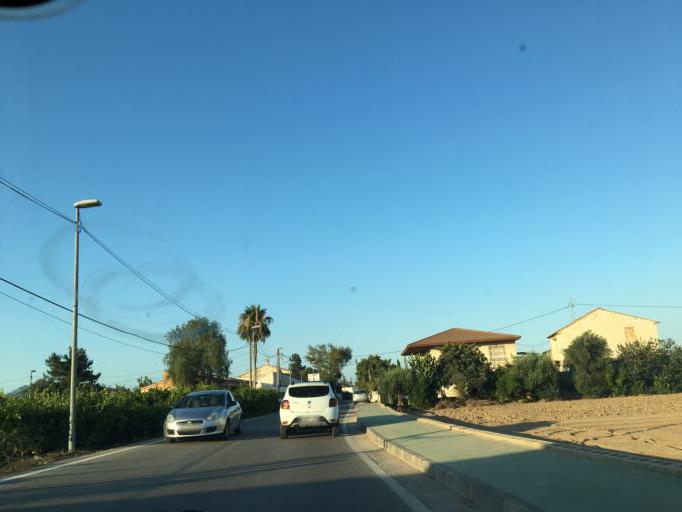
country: ES
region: Murcia
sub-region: Murcia
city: Santomera
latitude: 38.0127
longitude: -1.0632
